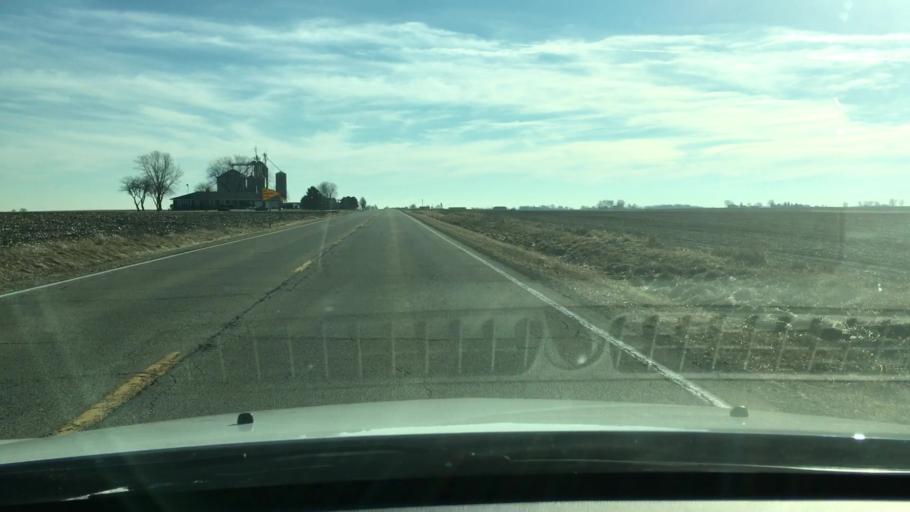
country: US
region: Illinois
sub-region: LaSalle County
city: Mendota
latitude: 41.5002
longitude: -89.1274
